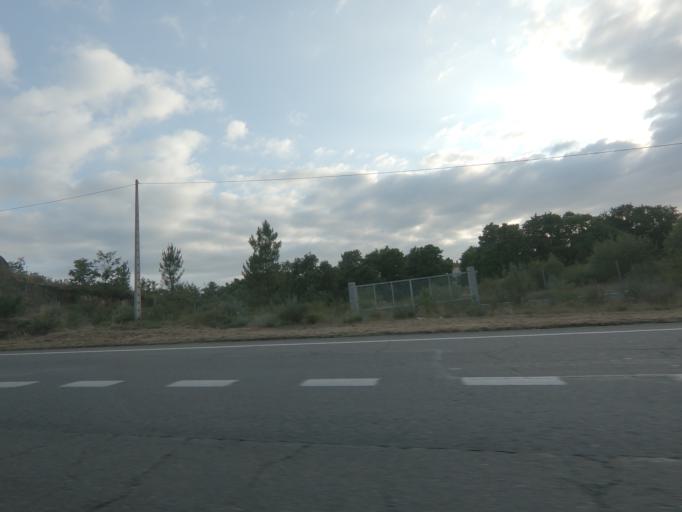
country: ES
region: Galicia
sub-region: Provincia de Ourense
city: Taboadela
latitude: 42.2714
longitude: -7.8377
